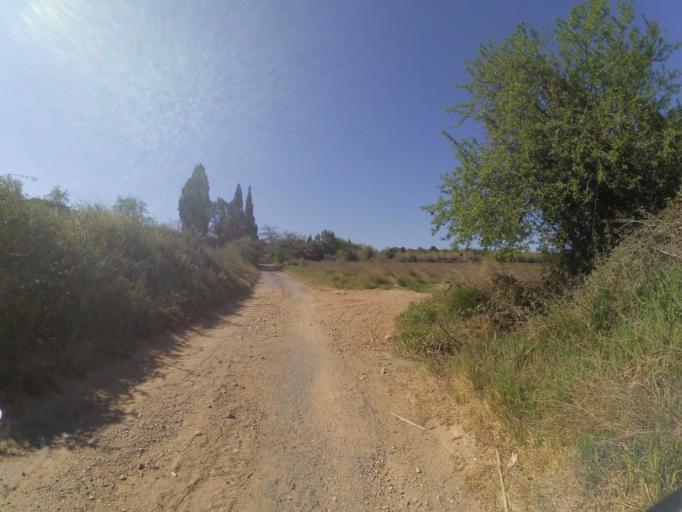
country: FR
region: Languedoc-Roussillon
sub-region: Departement des Pyrenees-Orientales
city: Baixas
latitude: 42.7421
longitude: 2.7988
